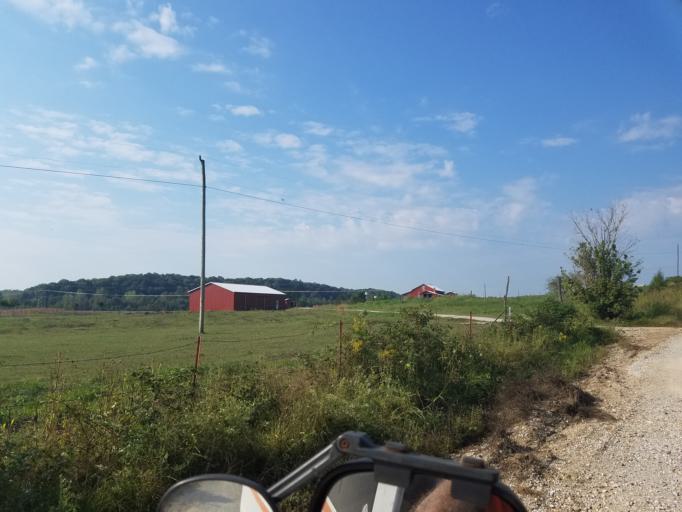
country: US
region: Missouri
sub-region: Moniteau County
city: California
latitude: 38.7349
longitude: -92.6162
